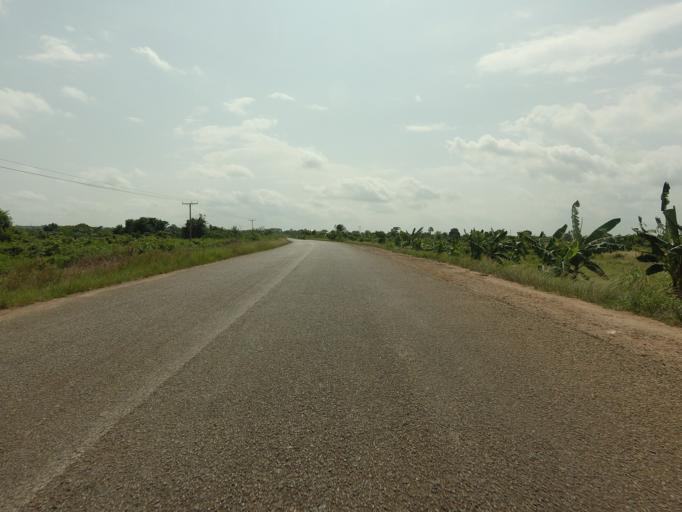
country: TG
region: Maritime
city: Lome
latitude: 6.2467
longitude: 0.9788
